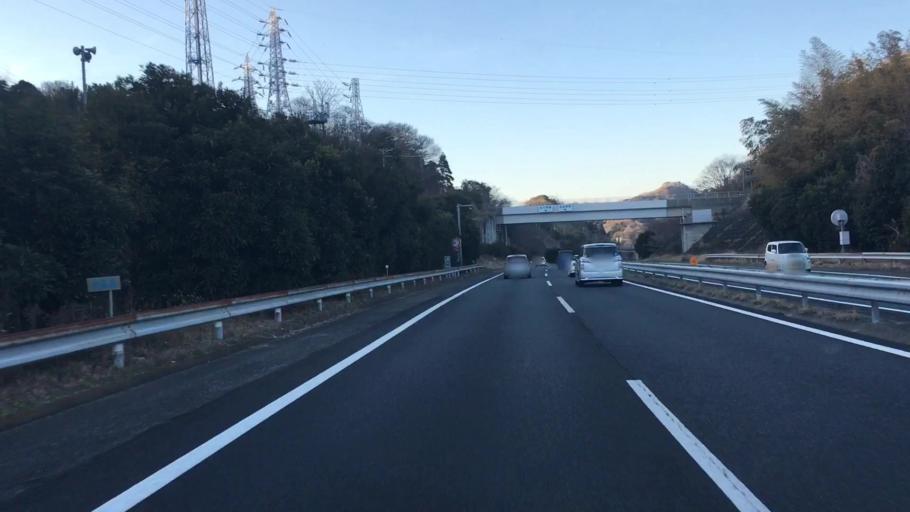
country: JP
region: Kanagawa
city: Yokosuka
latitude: 35.2575
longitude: 139.6352
